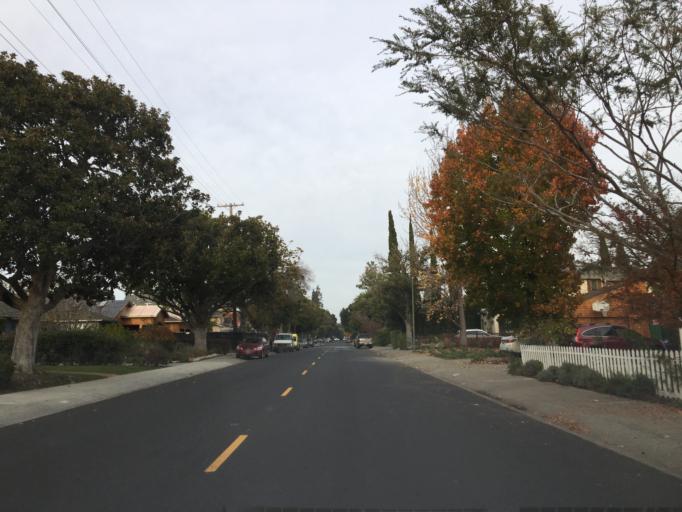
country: US
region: California
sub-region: Santa Clara County
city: Palo Alto
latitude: 37.4438
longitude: -122.1303
